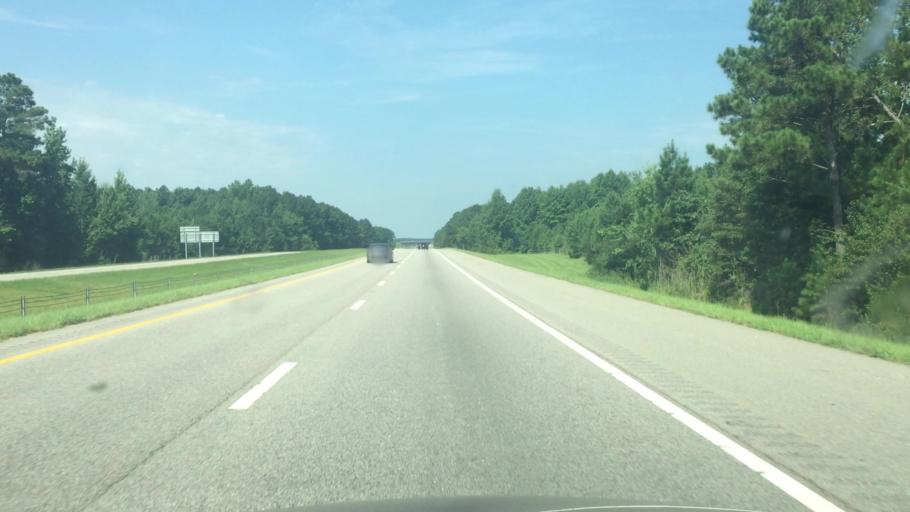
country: US
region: North Carolina
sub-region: Robeson County
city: Pembroke
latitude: 34.5980
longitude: -79.1533
